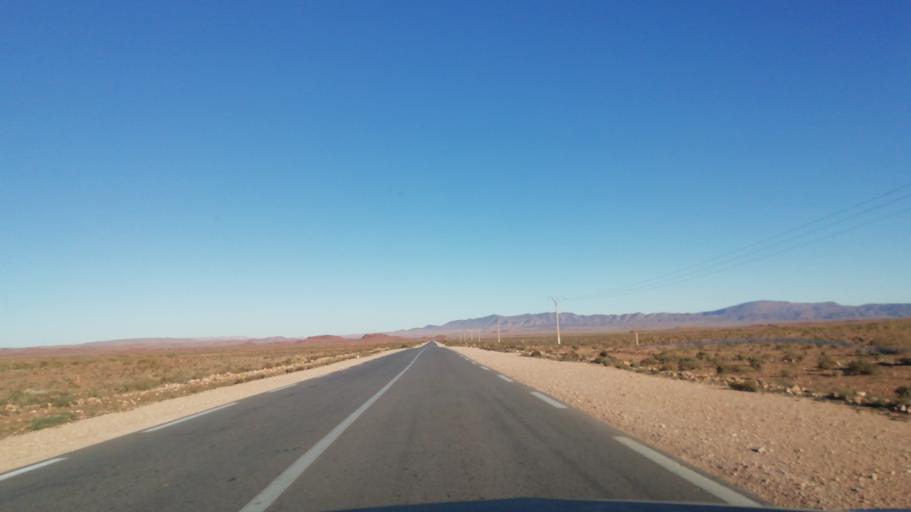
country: DZ
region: El Bayadh
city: El Abiodh Sidi Cheikh
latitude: 33.1675
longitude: 0.4712
